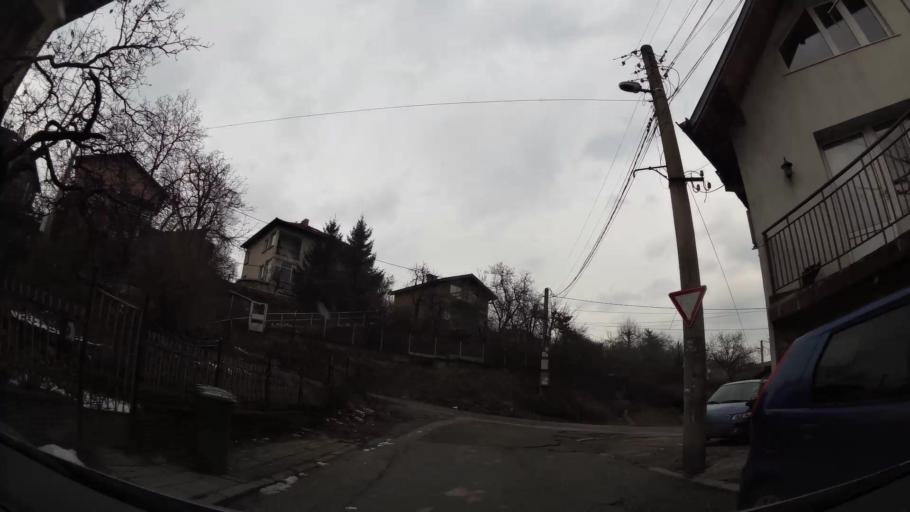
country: BG
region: Sofia-Capital
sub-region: Stolichna Obshtina
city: Sofia
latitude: 42.6614
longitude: 23.2419
